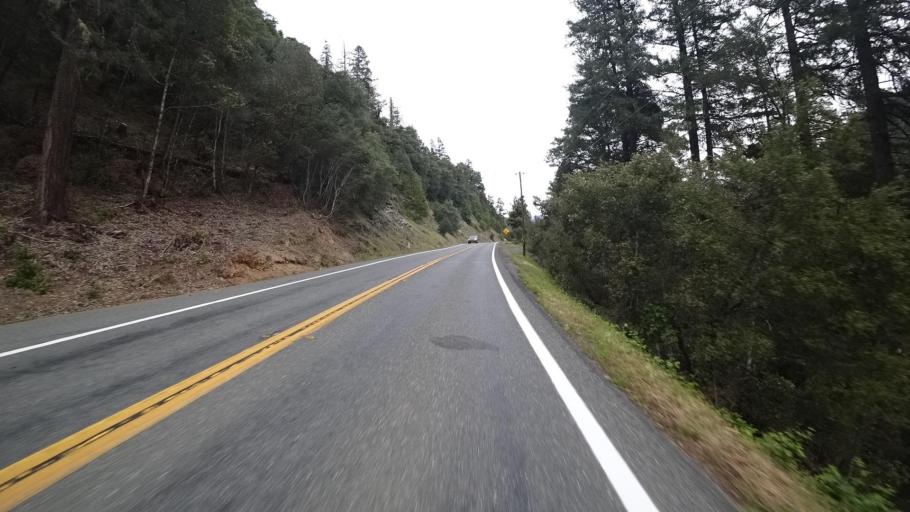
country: US
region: California
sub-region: Humboldt County
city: Willow Creek
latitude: 40.9964
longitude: -123.6290
